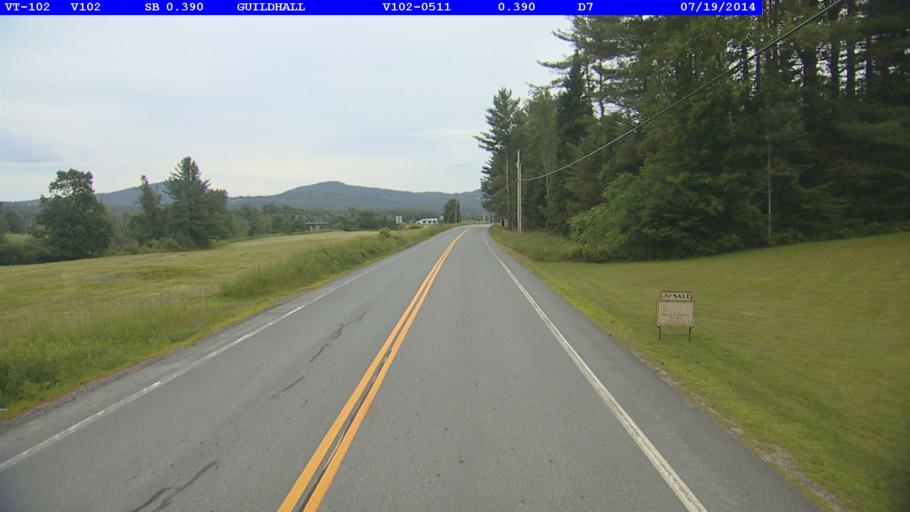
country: US
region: New Hampshire
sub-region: Coos County
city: Lancaster
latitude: 44.5011
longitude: -71.5953
